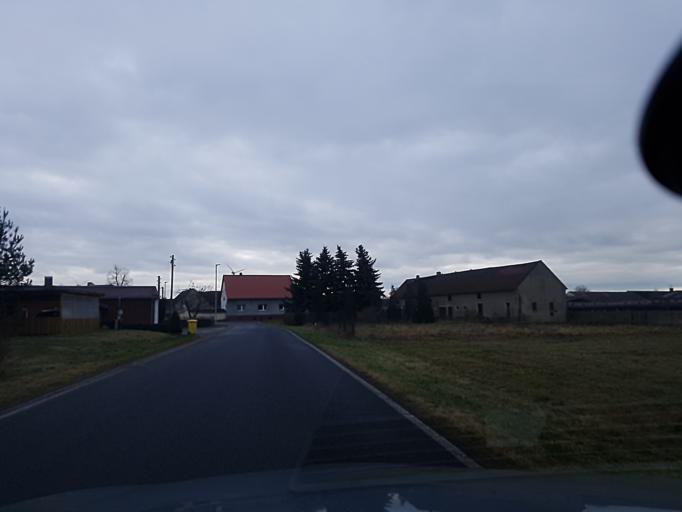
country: DE
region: Brandenburg
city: Bad Liebenwerda
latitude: 51.5497
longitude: 13.3360
